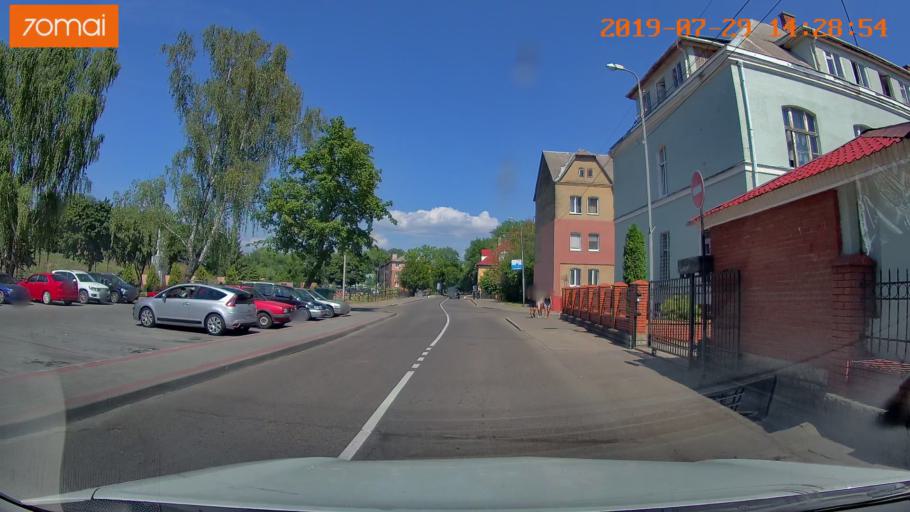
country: RU
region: Kaliningrad
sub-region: Gorod Kaliningrad
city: Baltiysk
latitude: 54.6410
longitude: 19.8903
